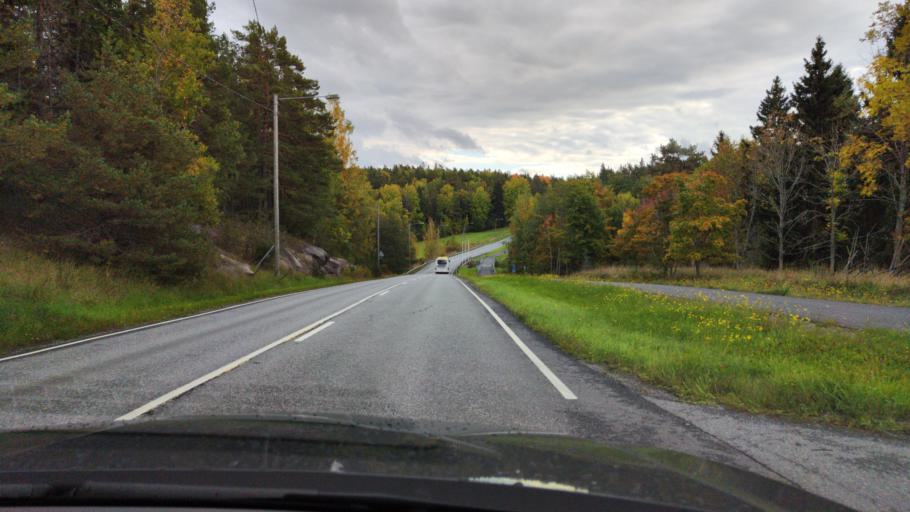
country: FI
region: Varsinais-Suomi
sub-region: Turku
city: Raisio
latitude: 60.3664
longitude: 22.1766
